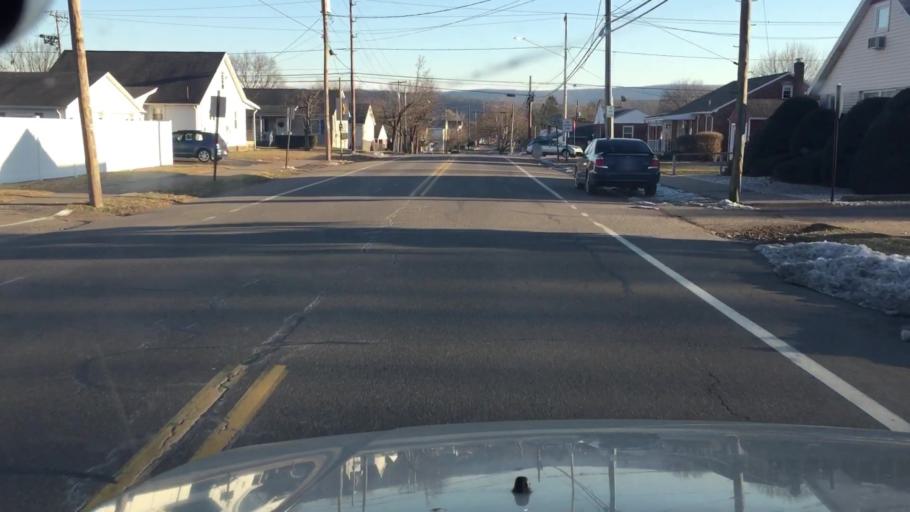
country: US
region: Pennsylvania
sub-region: Luzerne County
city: East Berwick
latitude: 41.0653
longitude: -76.2297
